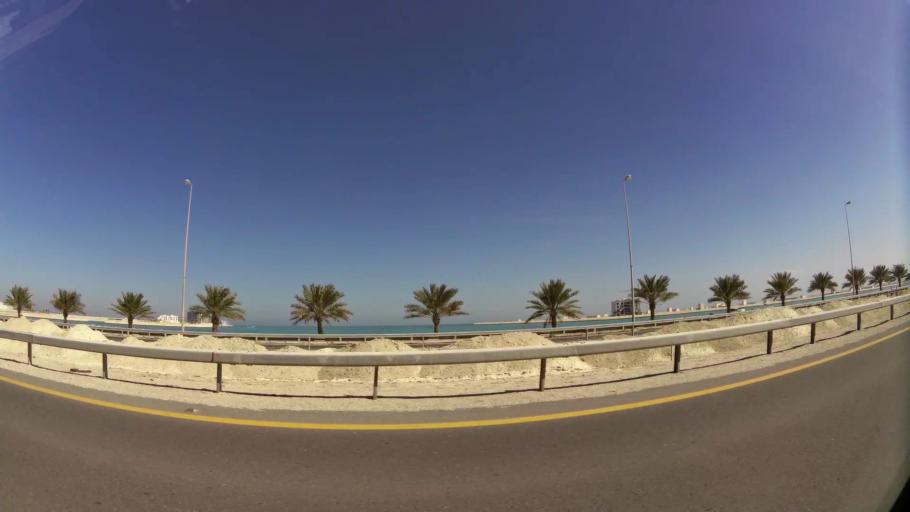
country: BH
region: Muharraq
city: Al Hadd
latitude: 26.2647
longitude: 50.6614
